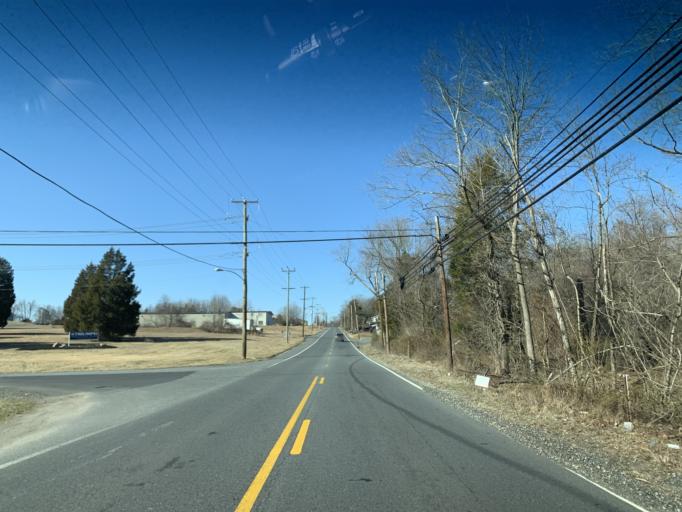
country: US
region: Maryland
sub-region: Cecil County
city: Elkton
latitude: 39.6164
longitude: -75.8491
